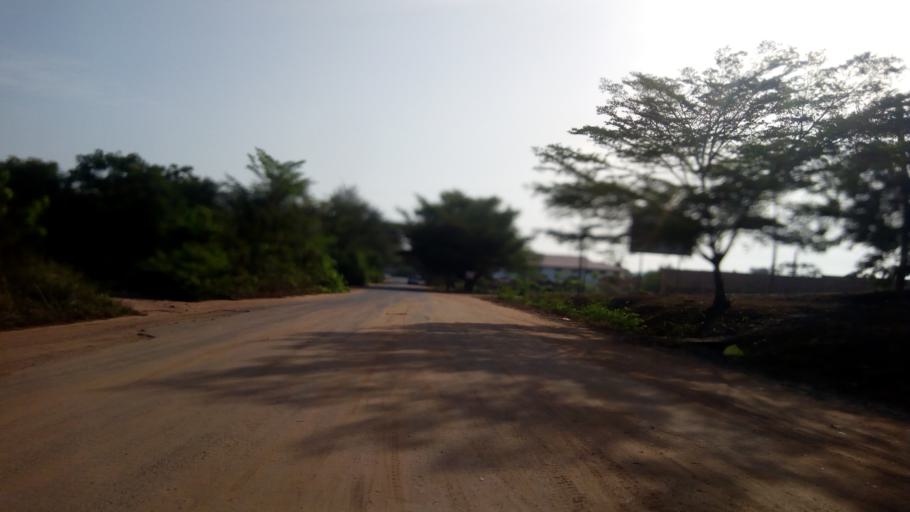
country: GH
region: Central
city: Cape Coast
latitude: 5.1157
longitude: -1.2737
